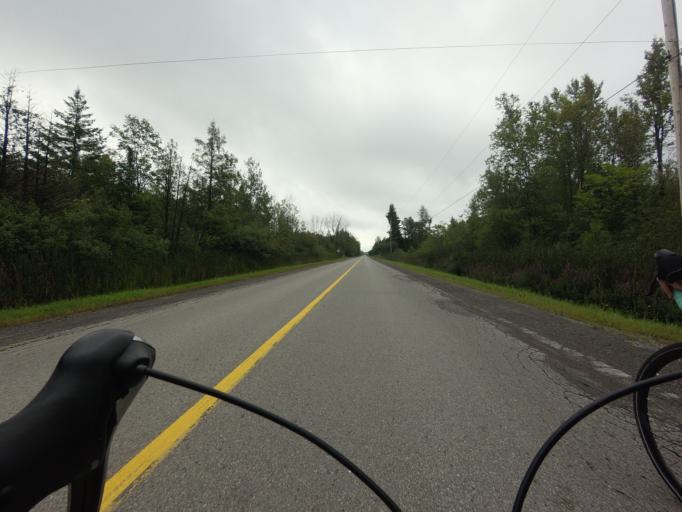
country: CA
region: Ontario
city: Bells Corners
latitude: 45.0783
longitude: -75.7422
